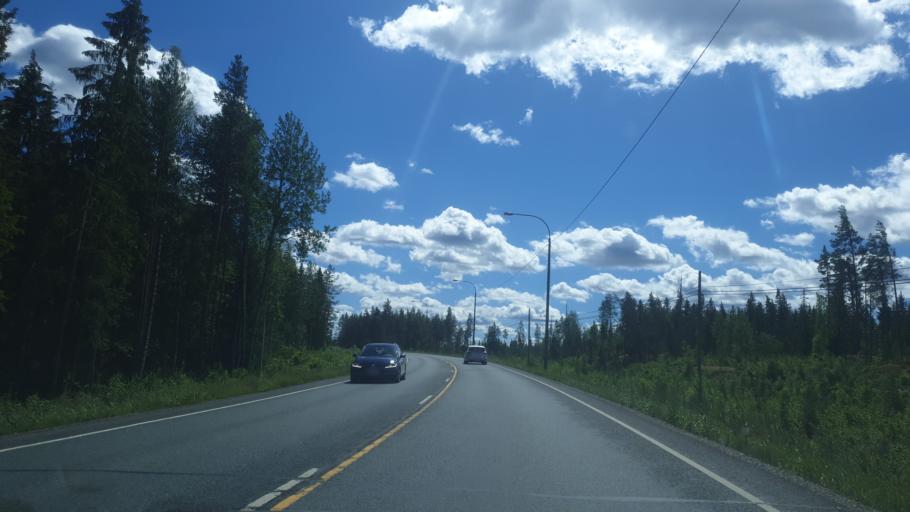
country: FI
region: Northern Savo
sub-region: Varkaus
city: Leppaevirta
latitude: 62.5696
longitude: 27.6110
